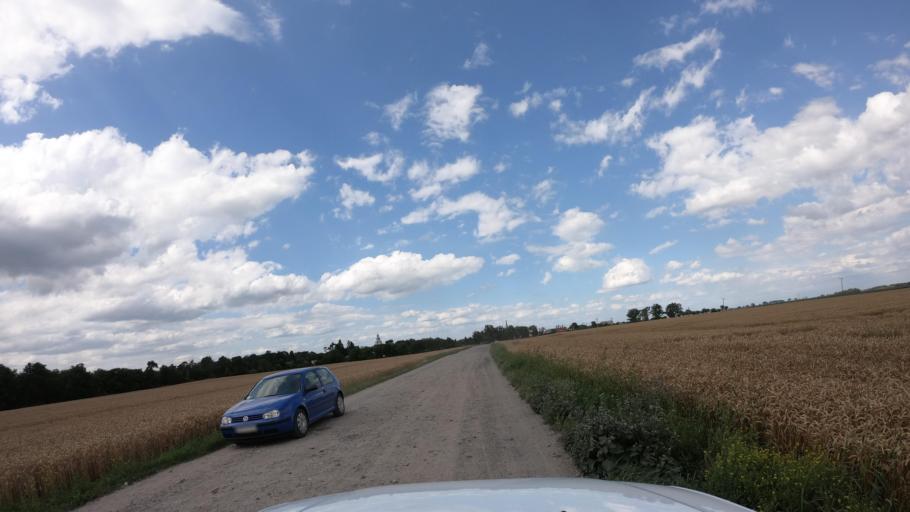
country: PL
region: West Pomeranian Voivodeship
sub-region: Powiat pyrzycki
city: Warnice
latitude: 53.2628
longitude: 14.9098
